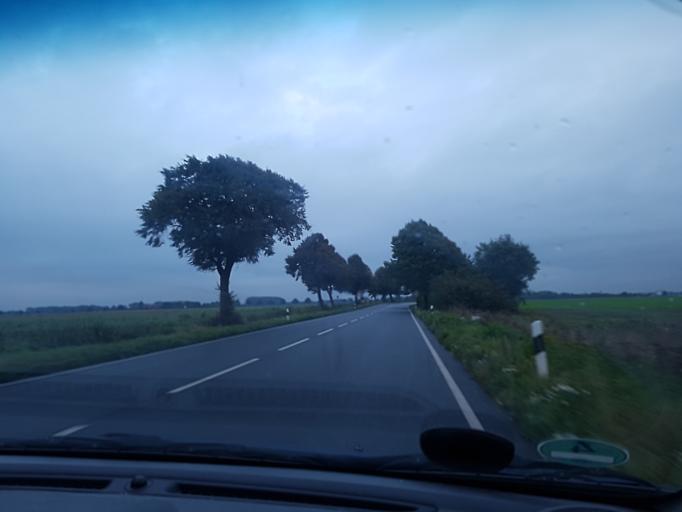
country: DE
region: Lower Saxony
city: Pattensen
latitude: 52.2865
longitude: 9.7553
